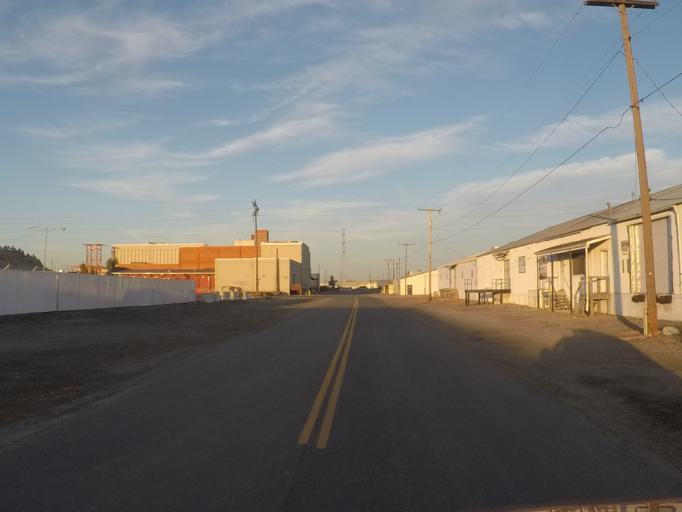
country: US
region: Montana
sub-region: Yellowstone County
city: Billings
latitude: 45.7883
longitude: -108.4901
